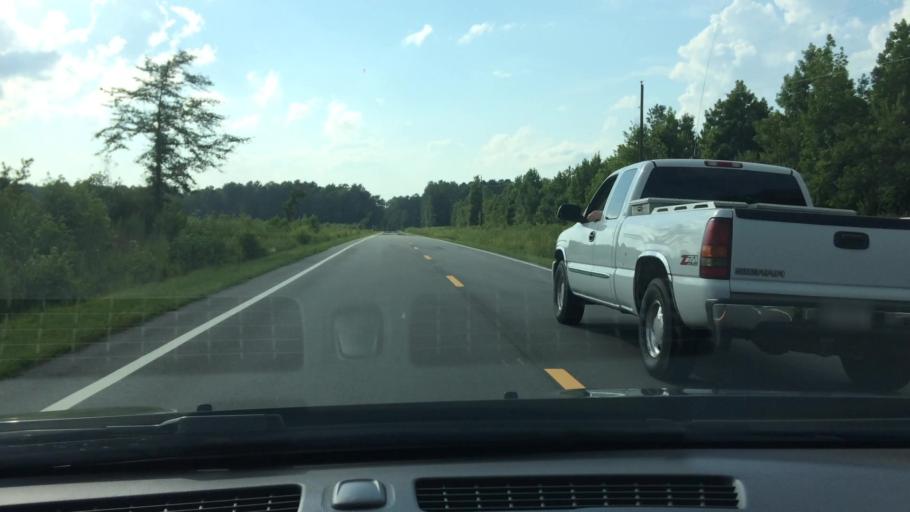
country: US
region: North Carolina
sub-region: Craven County
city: Vanceboro
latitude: 35.4352
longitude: -77.1381
